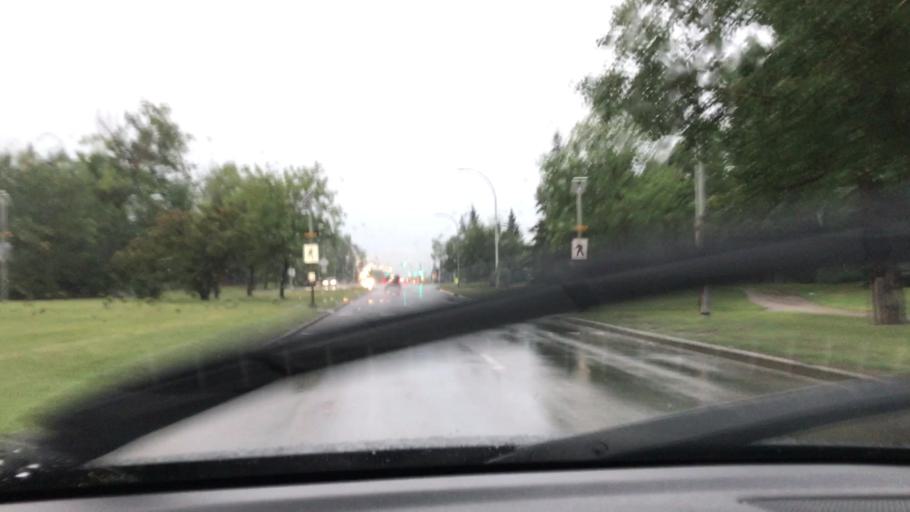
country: CA
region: Alberta
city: Sherwood Park
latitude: 53.5180
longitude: -113.3201
